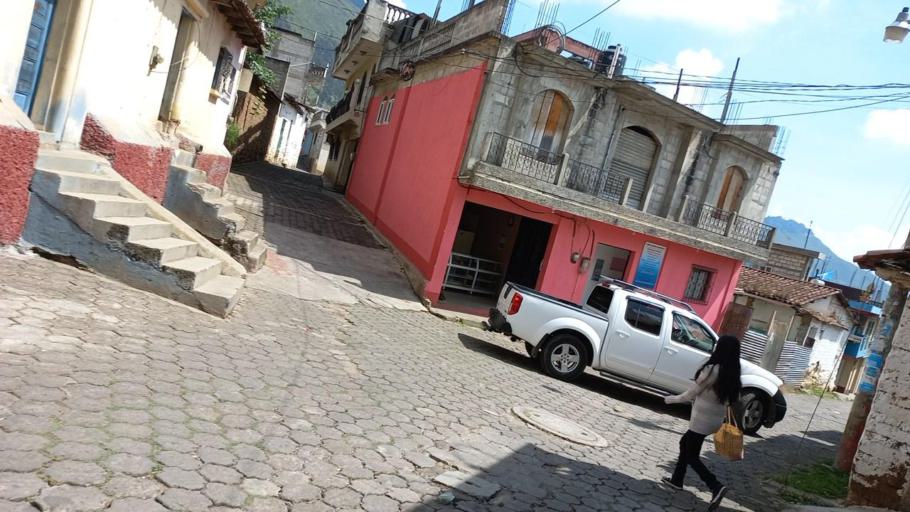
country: GT
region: Totonicapan
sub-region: Municipio de San Andres Xecul
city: San Andres Xecul
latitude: 14.9058
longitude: -91.4838
